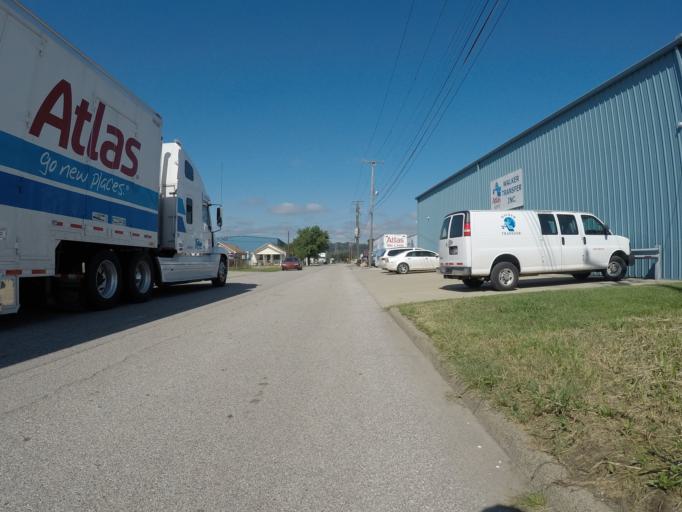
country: US
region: West Virginia
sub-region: Wayne County
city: Kenova
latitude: 38.4032
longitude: -82.5781
